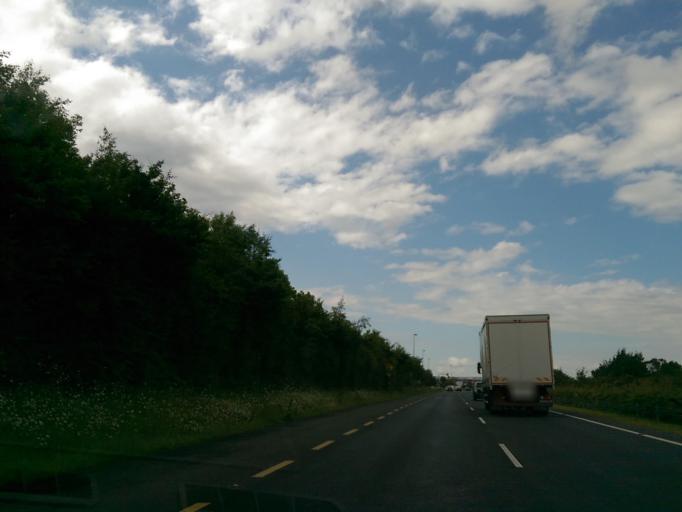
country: IE
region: Connaught
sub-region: County Galway
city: Claregalway
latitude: 53.2894
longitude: -8.9837
